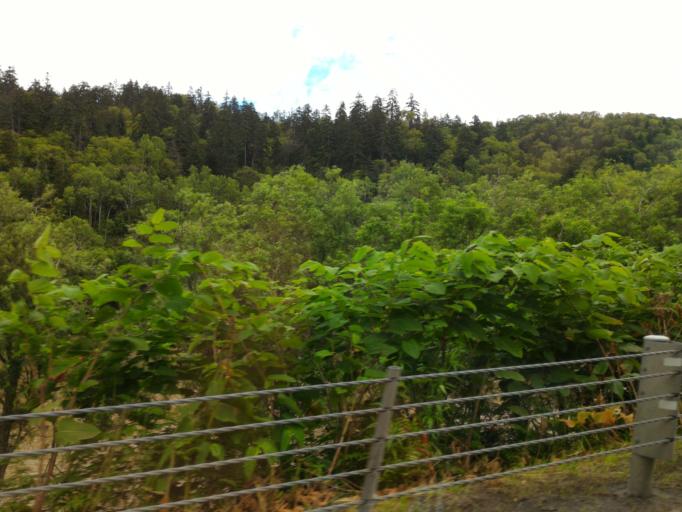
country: JP
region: Hokkaido
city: Nayoro
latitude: 44.7259
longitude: 142.2331
